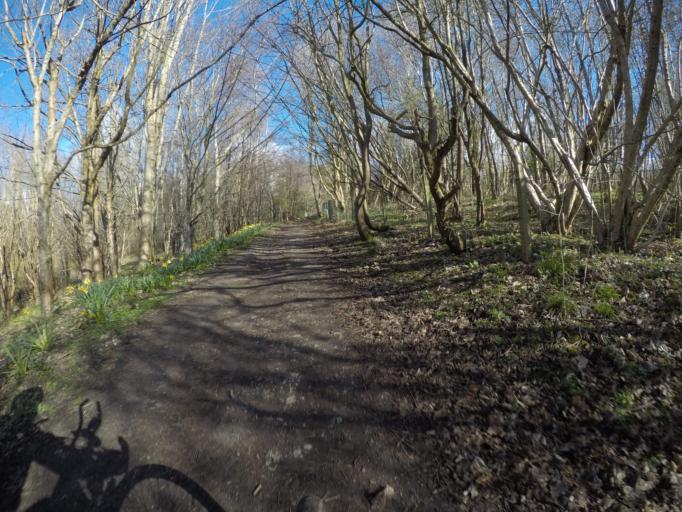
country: GB
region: Scotland
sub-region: North Ayrshire
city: Irvine
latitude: 55.6477
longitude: -4.6596
